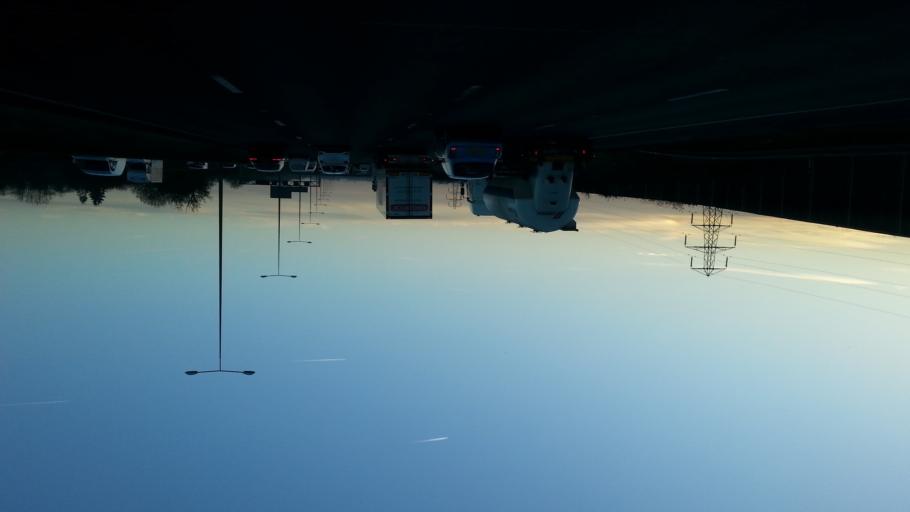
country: GB
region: England
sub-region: Hertfordshire
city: Redbourn
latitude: 51.8080
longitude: -0.4148
